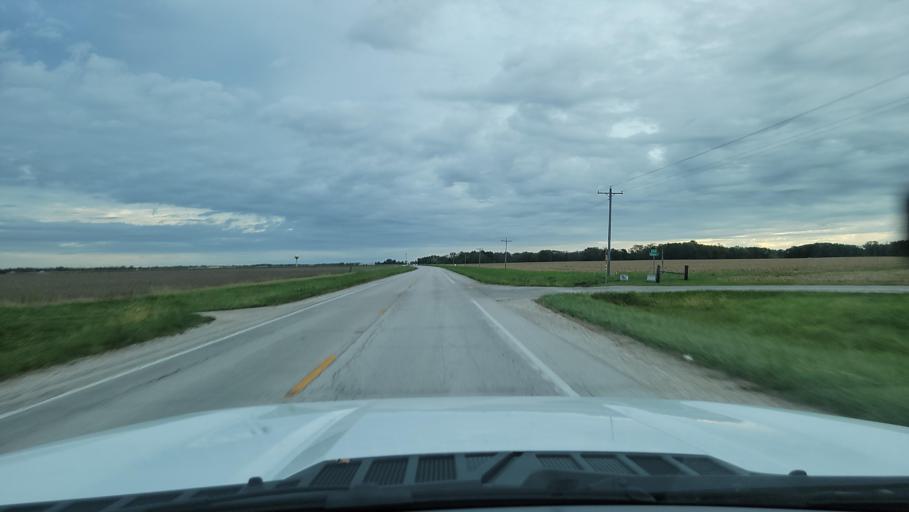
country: US
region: Illinois
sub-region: Schuyler County
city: Rushville
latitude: 40.1018
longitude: -90.5965
